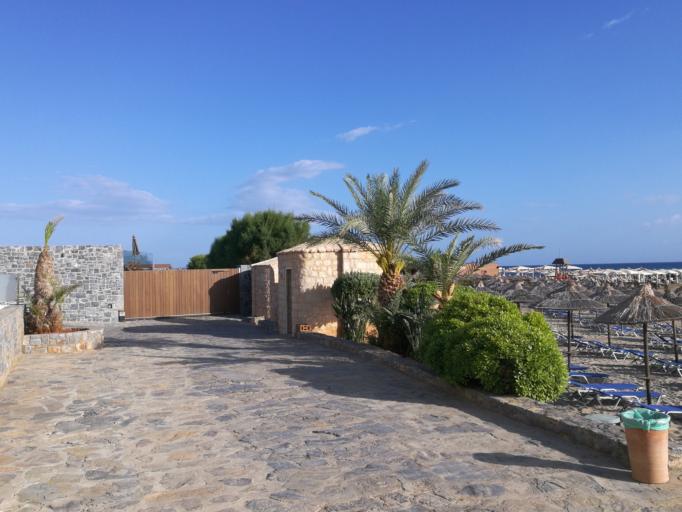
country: GR
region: Crete
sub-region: Nomos Irakleiou
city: Stalis
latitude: 35.3050
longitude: 25.4206
